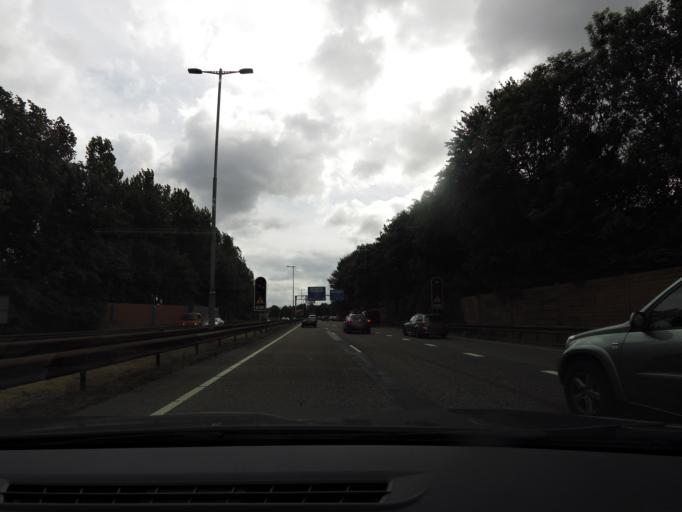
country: NL
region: Utrecht
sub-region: Gemeente Utrecht
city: Lunetten
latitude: 52.0603
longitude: 5.1239
